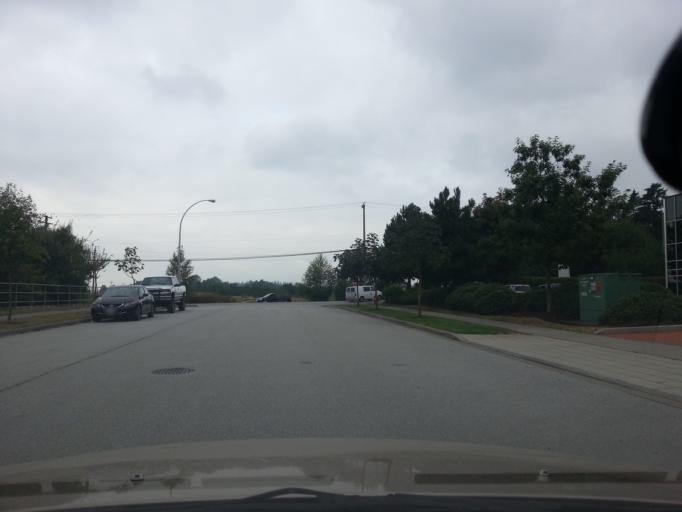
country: CA
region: British Columbia
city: Langley
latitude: 49.0991
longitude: -122.7118
